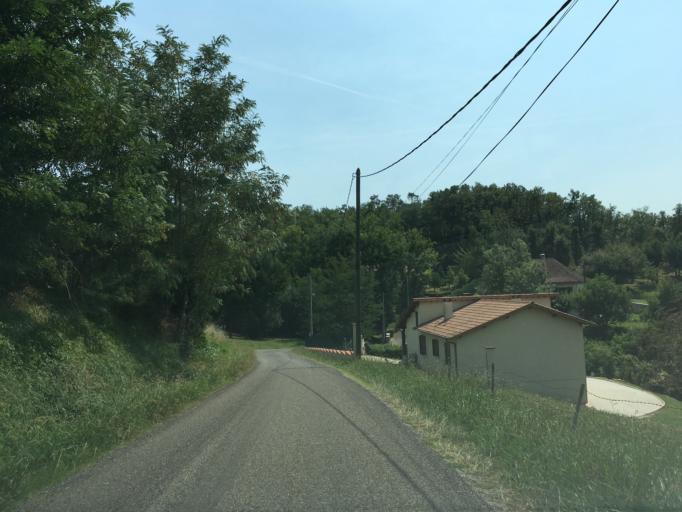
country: FR
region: Midi-Pyrenees
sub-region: Departement du Tarn-et-Garonne
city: Saint-Nauphary
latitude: 43.9919
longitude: 1.4036
